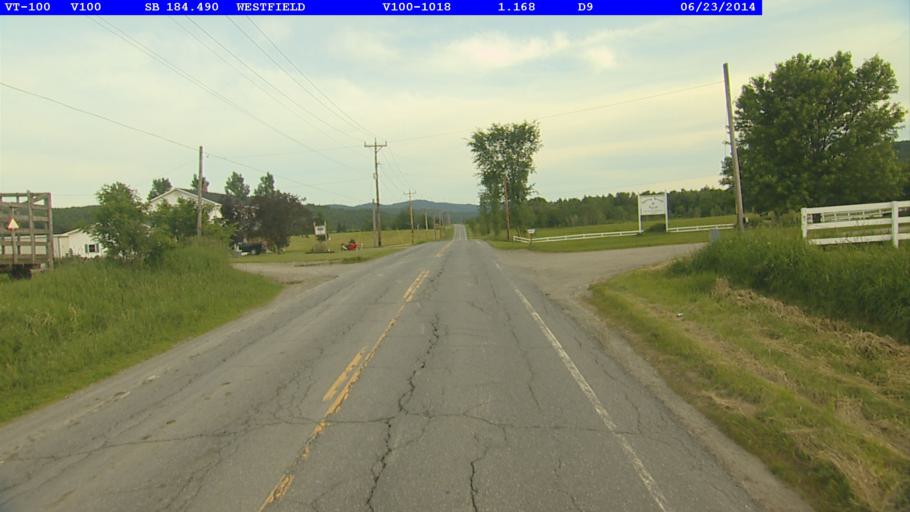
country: US
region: Vermont
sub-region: Orleans County
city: Newport
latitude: 44.8517
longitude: -72.4341
